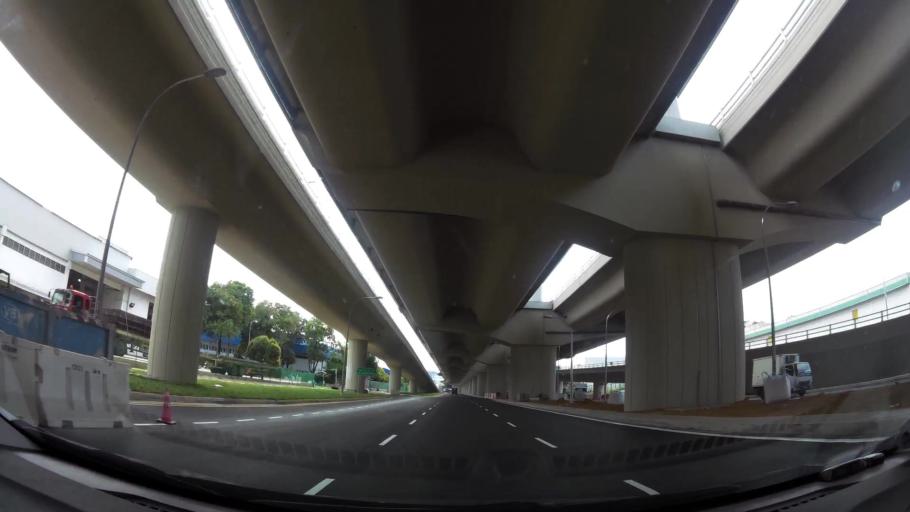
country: MY
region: Johor
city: Johor Bahru
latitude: 1.3253
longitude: 103.6447
